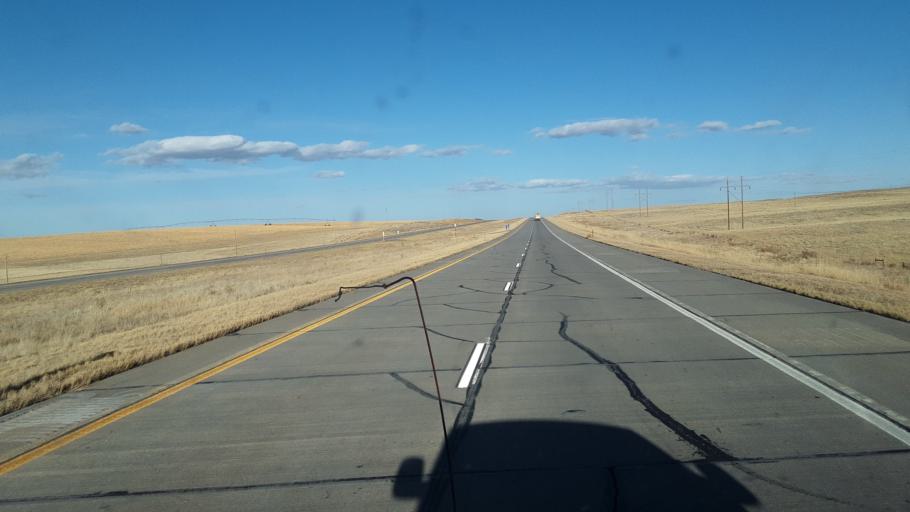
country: US
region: Colorado
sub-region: Logan County
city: Sterling
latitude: 40.7434
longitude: -102.9959
